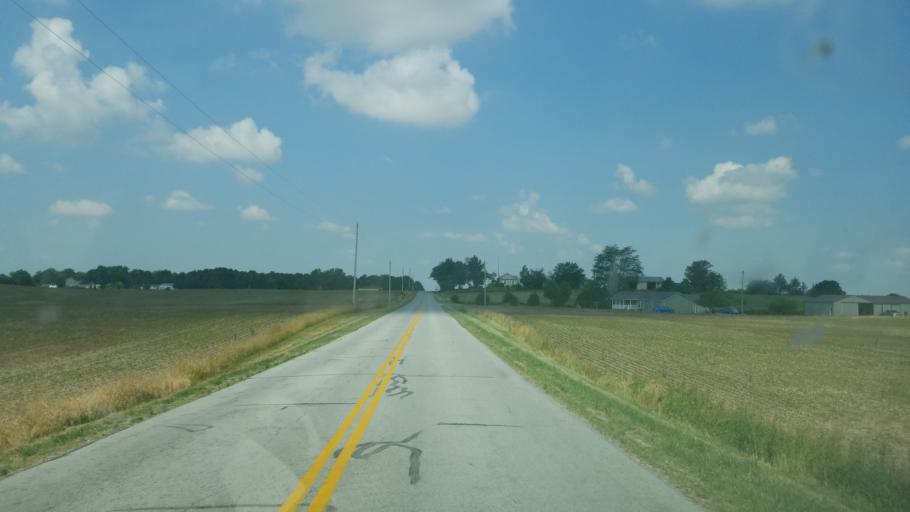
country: US
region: Ohio
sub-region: Auglaize County
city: Cridersville
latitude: 40.5714
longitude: -84.0535
